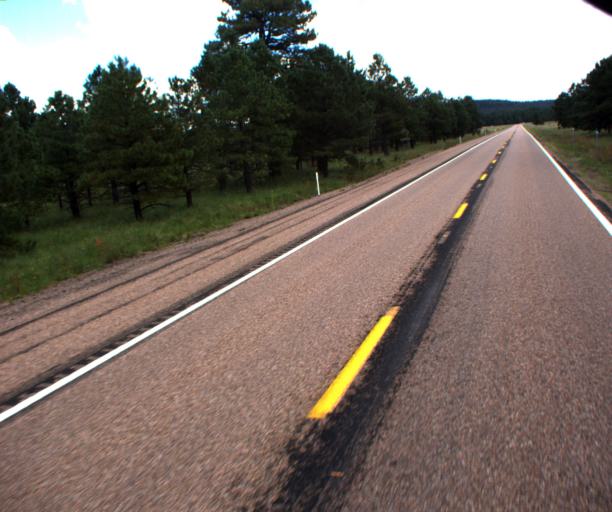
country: US
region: Arizona
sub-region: Navajo County
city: Pinetop-Lakeside
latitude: 34.0438
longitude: -109.6894
